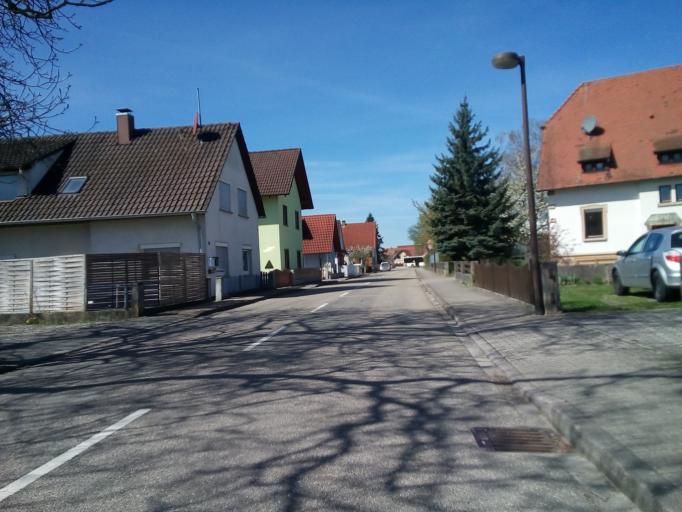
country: DE
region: Baden-Wuerttemberg
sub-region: Freiburg Region
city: Rheinau
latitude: 48.6523
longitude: 7.9296
